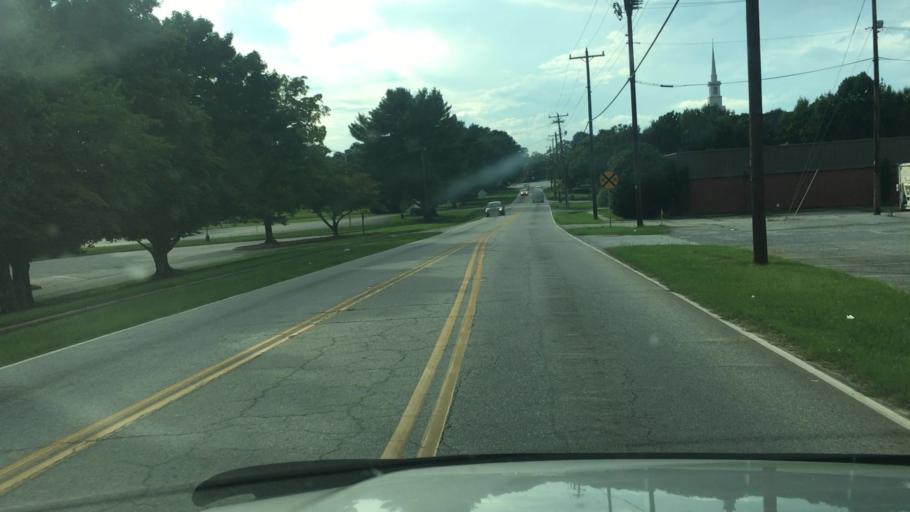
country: US
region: South Carolina
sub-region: Spartanburg County
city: Spartanburg
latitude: 34.9733
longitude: -81.9303
